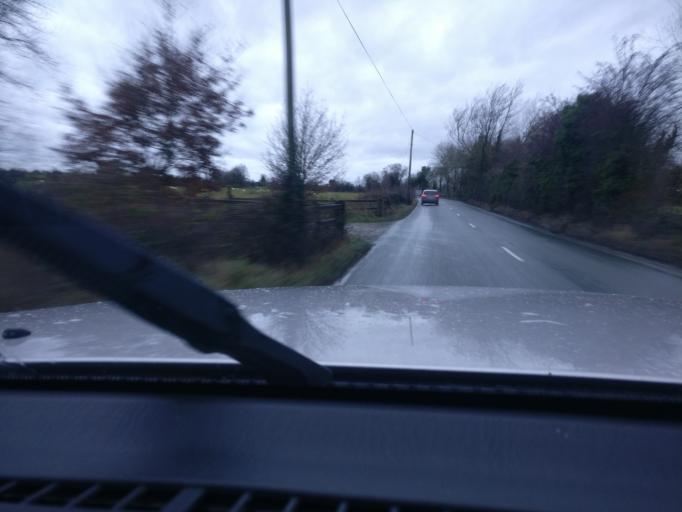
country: IE
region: Leinster
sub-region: An Mhi
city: Longwood
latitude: 53.4757
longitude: -6.9030
